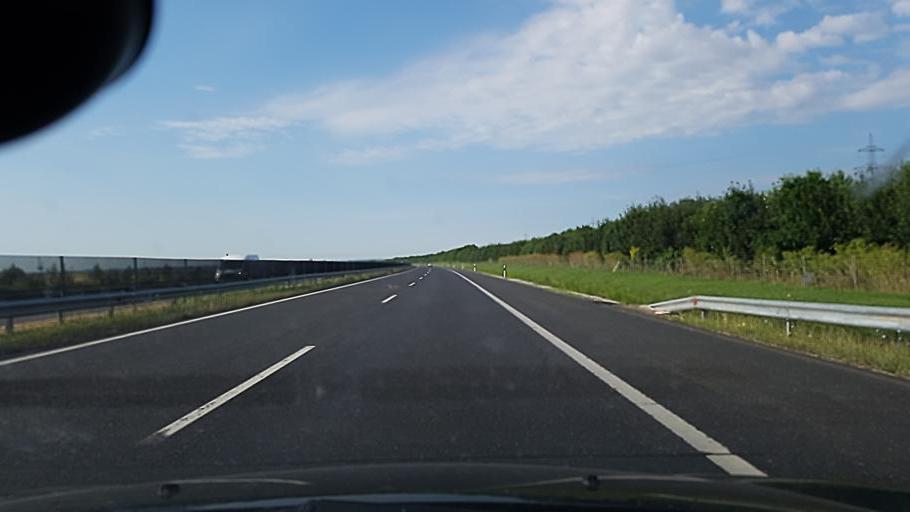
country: HU
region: Fejer
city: Ivancsa
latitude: 47.1627
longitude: 18.8032
